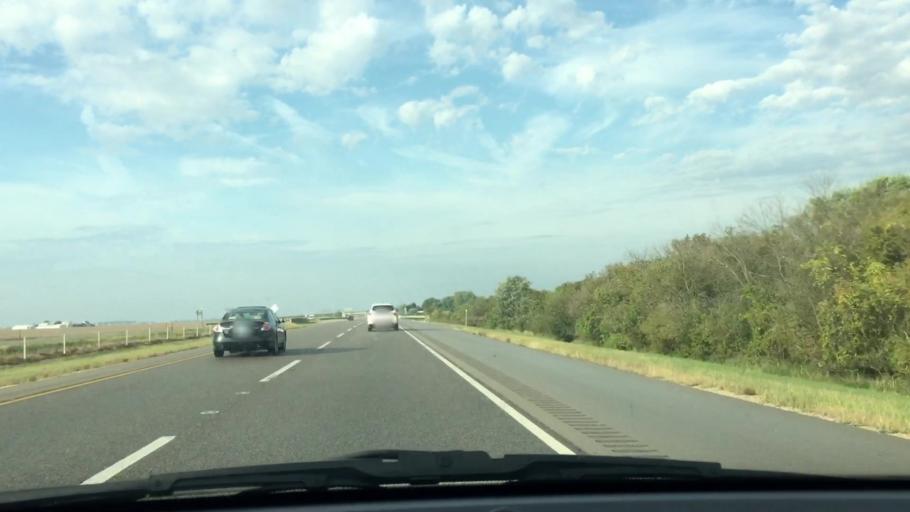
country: US
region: Illinois
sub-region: Ogle County
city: Rochelle
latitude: 41.8895
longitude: -89.0985
